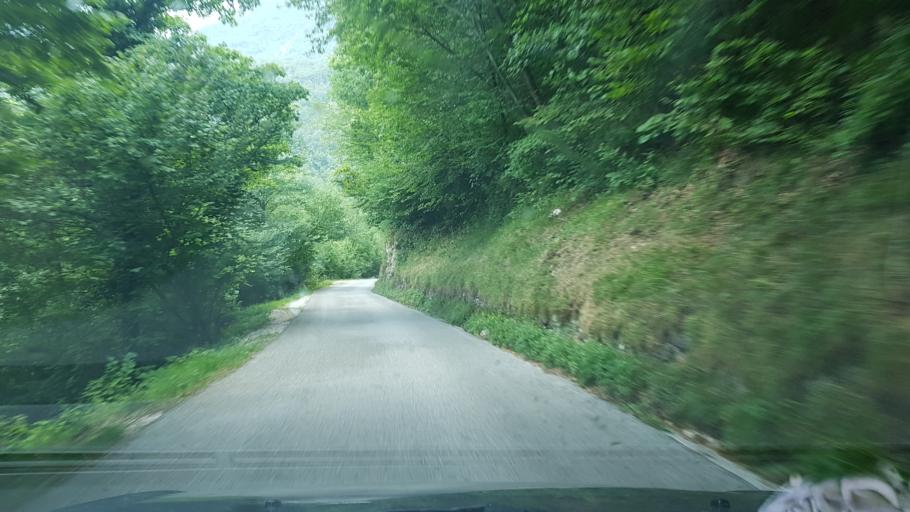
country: IT
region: Veneto
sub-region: Provincia di Vicenza
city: Recoaro Terme
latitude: 45.7648
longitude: 11.1985
